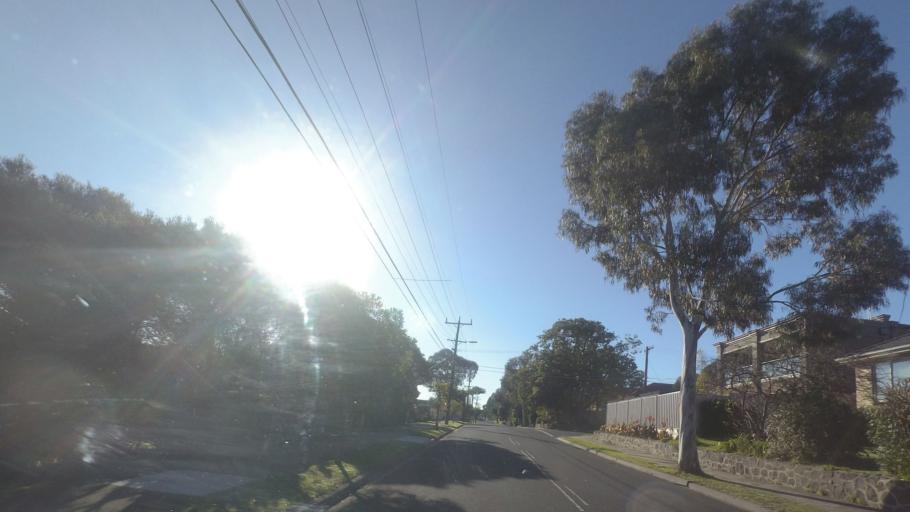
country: AU
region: Victoria
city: Watsonia
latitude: -37.7216
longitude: 145.0752
